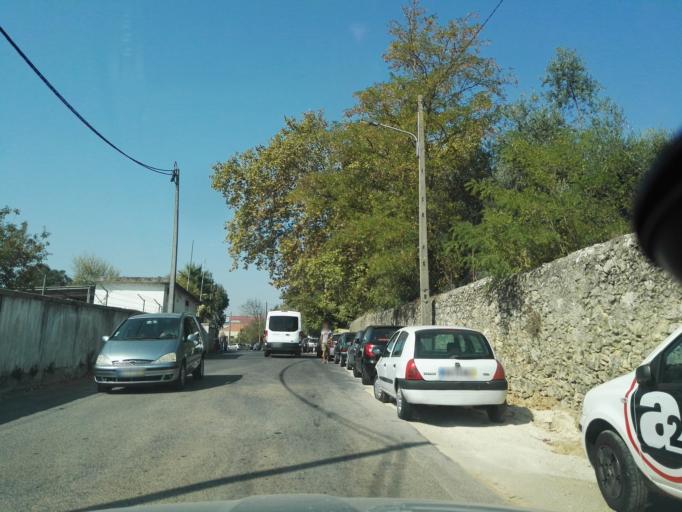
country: PT
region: Lisbon
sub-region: Loures
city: Camarate
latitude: 38.7836
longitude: -9.1278
